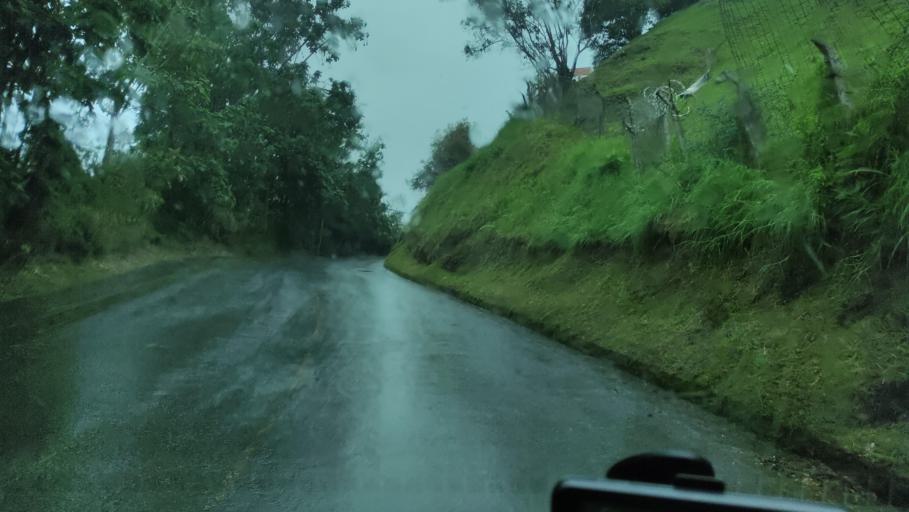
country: CO
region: Caldas
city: Villamaria
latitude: 5.0531
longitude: -75.4760
